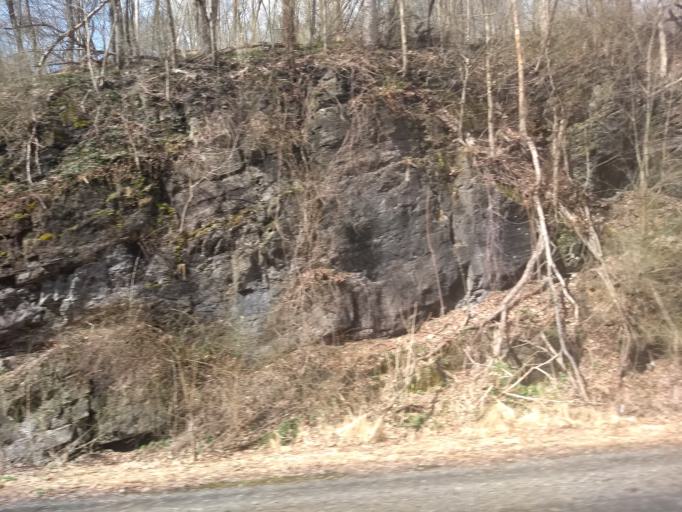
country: US
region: Pennsylvania
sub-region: Blair County
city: Tyrone
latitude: 40.6436
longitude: -78.1974
